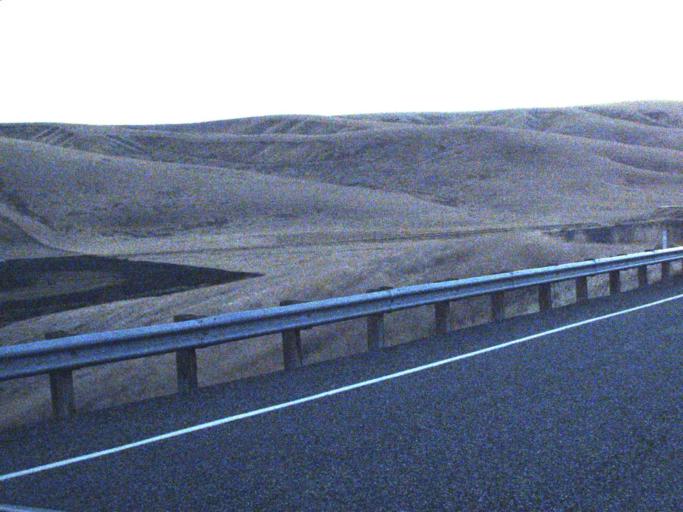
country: US
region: Washington
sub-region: Garfield County
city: Pomeroy
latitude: 46.5249
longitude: -117.8071
